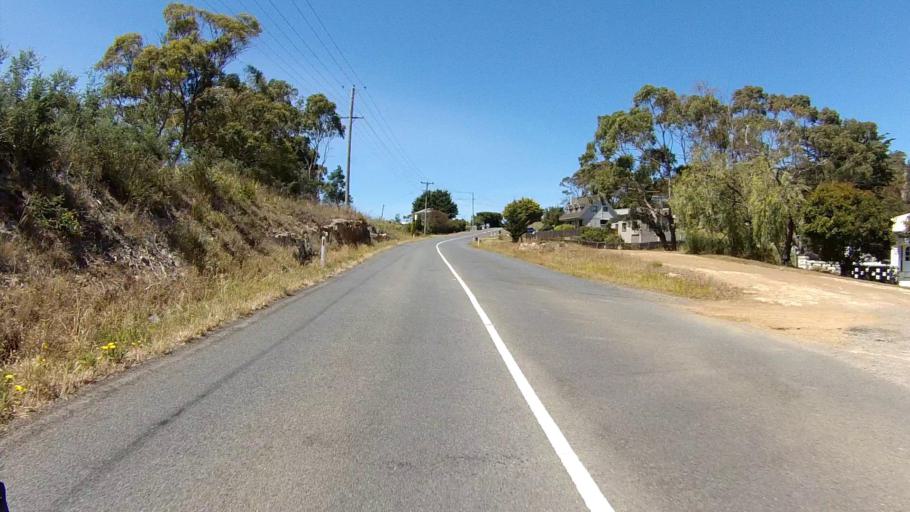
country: AU
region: Tasmania
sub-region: Clarence
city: Howrah
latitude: -42.8587
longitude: 147.4146
